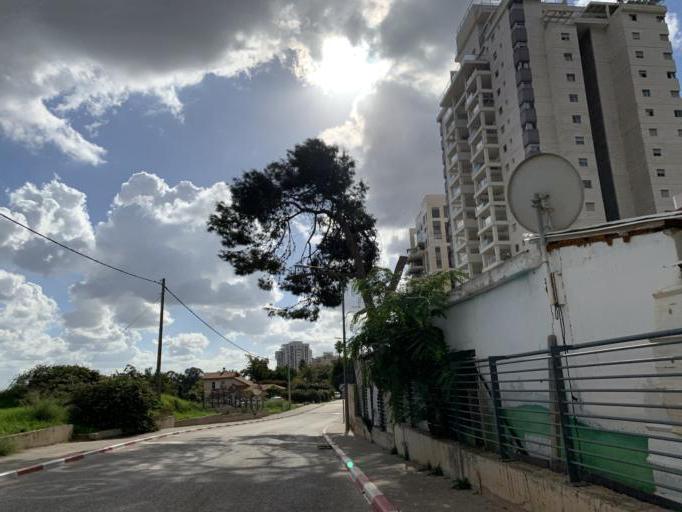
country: IL
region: Central District
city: Hod HaSharon
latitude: 32.1619
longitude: 34.8962
